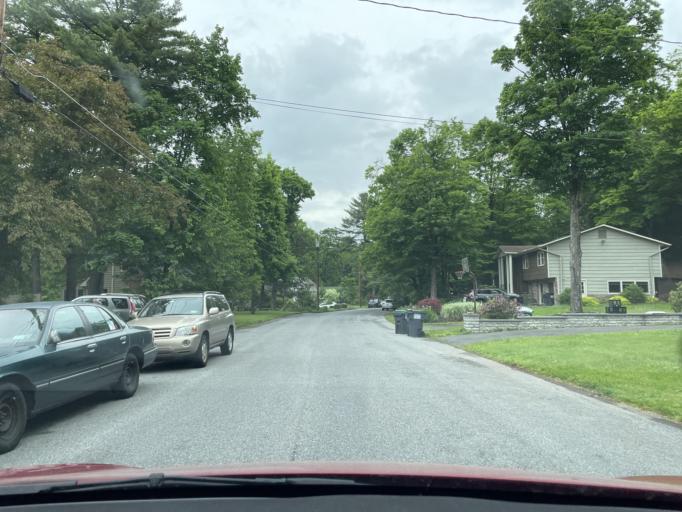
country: US
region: New York
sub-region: Ulster County
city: New Paltz
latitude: 41.7490
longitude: -74.0777
